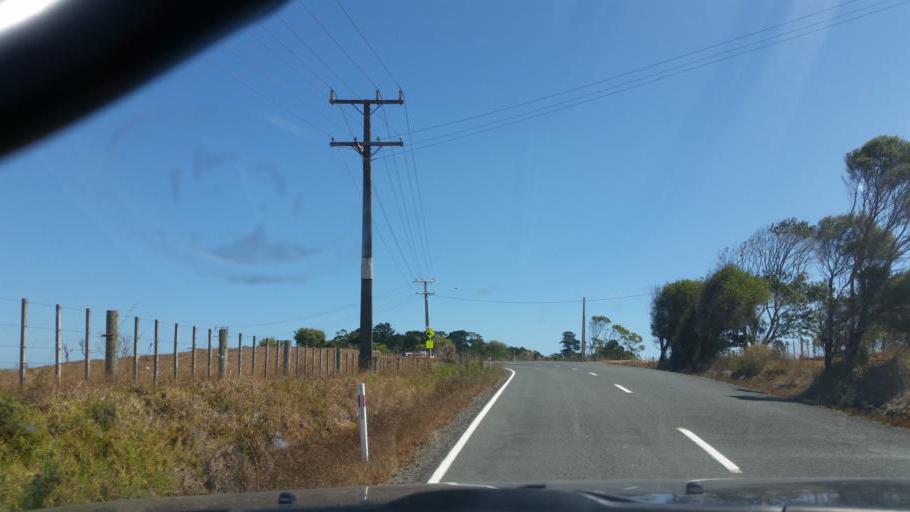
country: NZ
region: Northland
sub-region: Kaipara District
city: Dargaville
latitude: -36.0068
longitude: 173.9466
